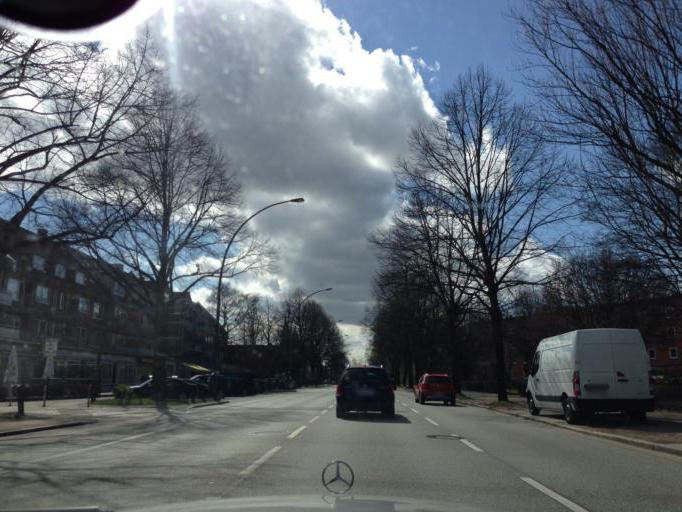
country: DE
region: Hamburg
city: Wandsbek
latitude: 53.5464
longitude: 10.1061
